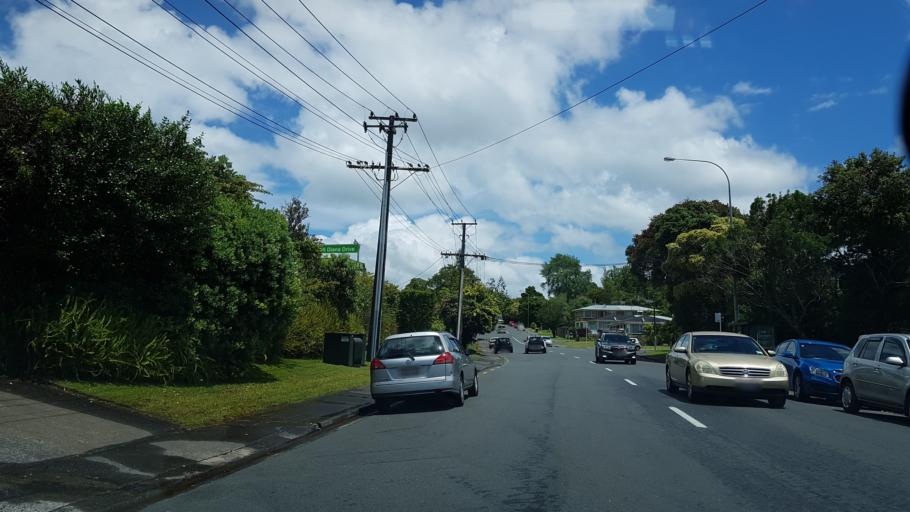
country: NZ
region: Auckland
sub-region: Auckland
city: North Shore
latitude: -36.7758
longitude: 174.7325
